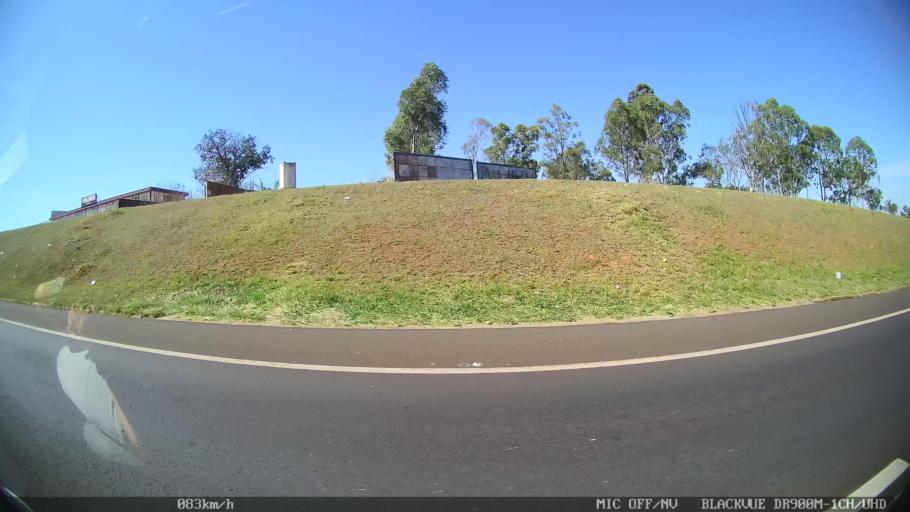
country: BR
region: Sao Paulo
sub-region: Franca
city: Franca
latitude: -20.5313
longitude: -47.4239
